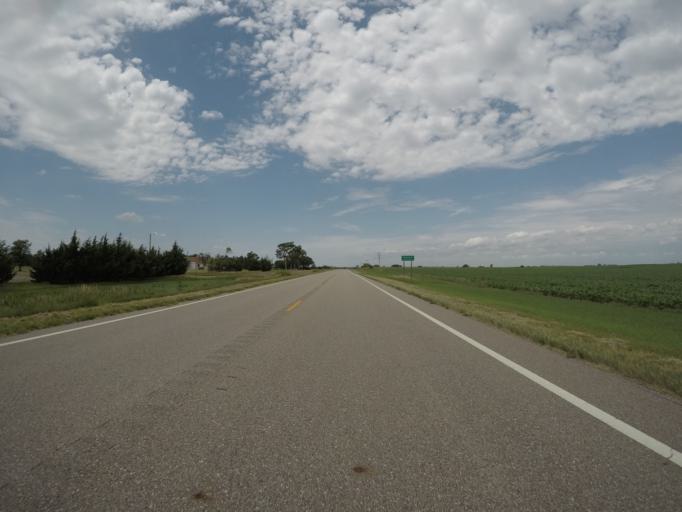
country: US
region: Kansas
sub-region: Graham County
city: Hill City
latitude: 39.3944
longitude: -99.6127
